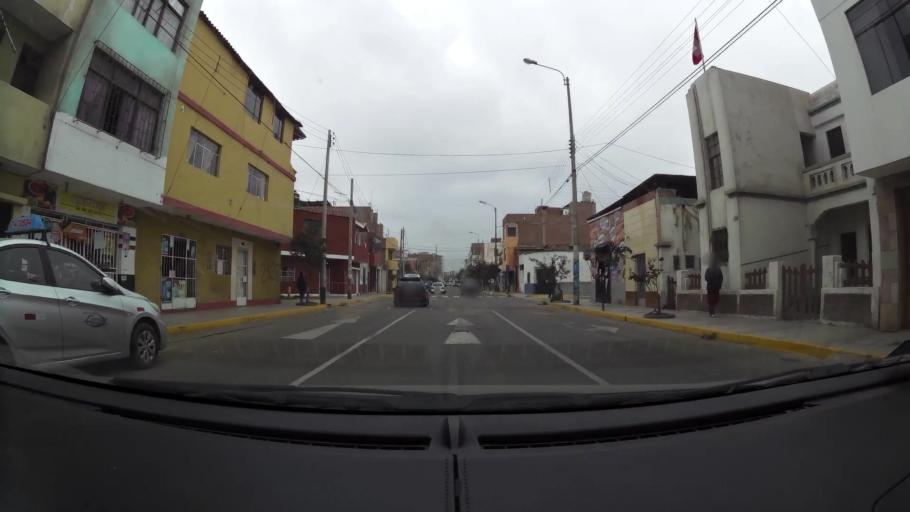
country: PE
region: La Libertad
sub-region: Provincia de Trujillo
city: Trujillo
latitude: -8.1206
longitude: -79.0241
